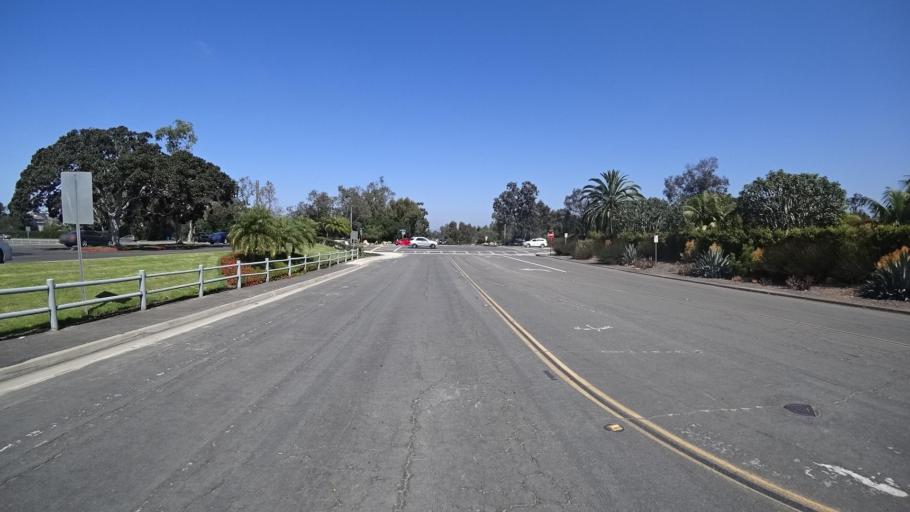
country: US
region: California
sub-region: San Diego County
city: Solana Beach
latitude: 32.9954
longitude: -117.2388
